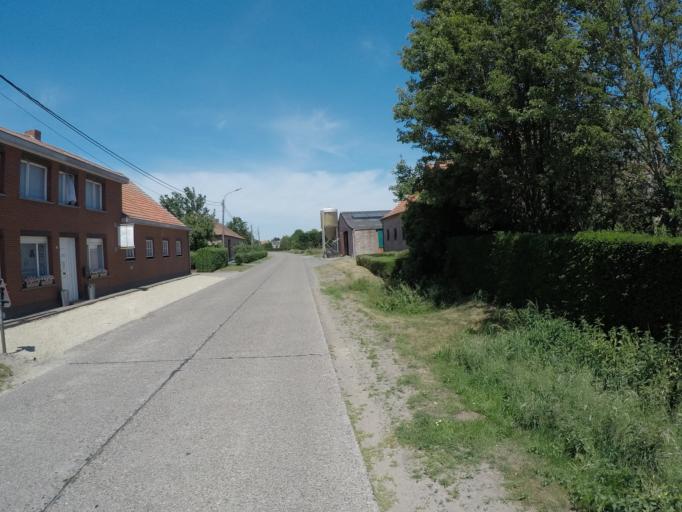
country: BE
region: Flanders
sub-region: Provincie Antwerpen
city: Wuustwezel
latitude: 51.3886
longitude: 4.6334
